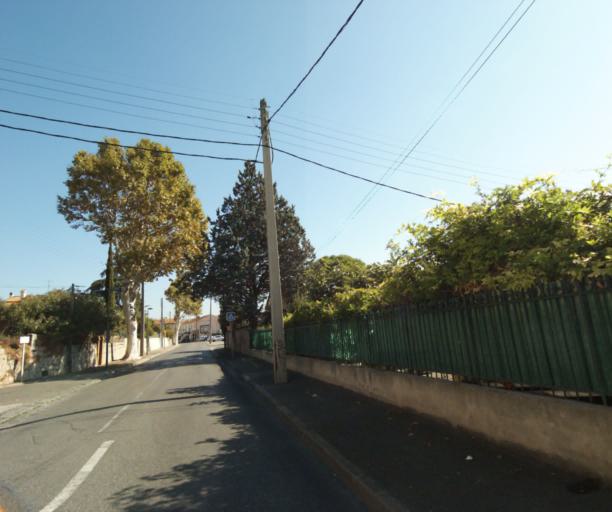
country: FR
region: Provence-Alpes-Cote d'Azur
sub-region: Departement des Bouches-du-Rhone
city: Plan-de-Cuques
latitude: 43.3396
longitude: 5.4549
